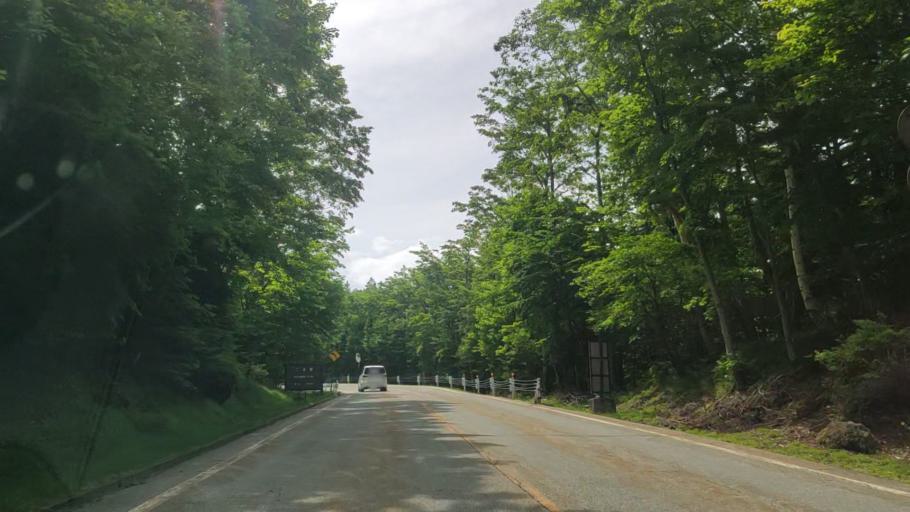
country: JP
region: Yamanashi
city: Fujikawaguchiko
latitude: 35.4154
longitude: 138.7161
